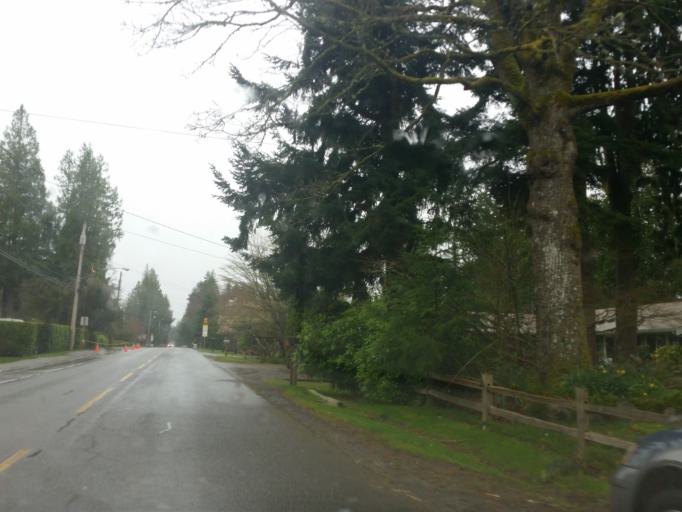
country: US
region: Washington
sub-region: Snohomish County
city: Meadowdale
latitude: 47.8284
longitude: -122.3468
